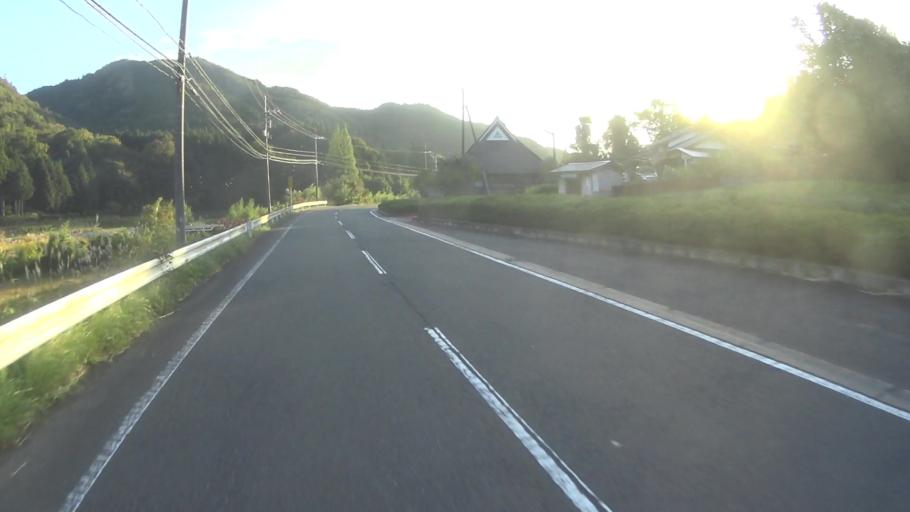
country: JP
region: Kyoto
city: Ayabe
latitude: 35.2334
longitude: 135.2541
